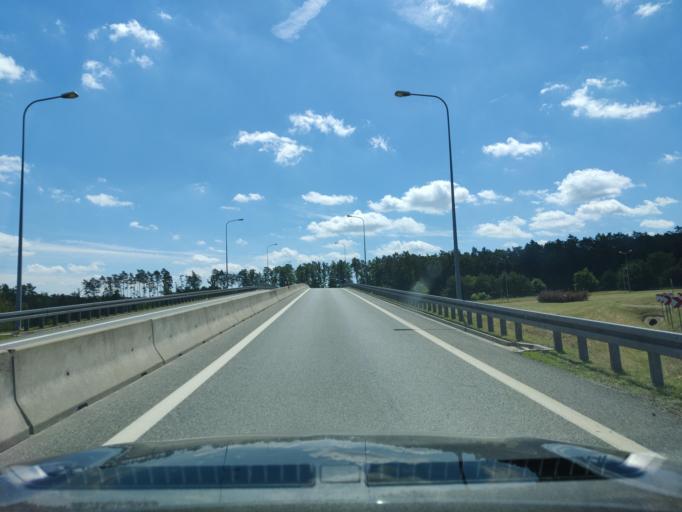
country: PL
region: Greater Poland Voivodeship
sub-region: Powiat nowotomyski
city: Nowy Tomysl
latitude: 52.3601
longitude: 16.1004
